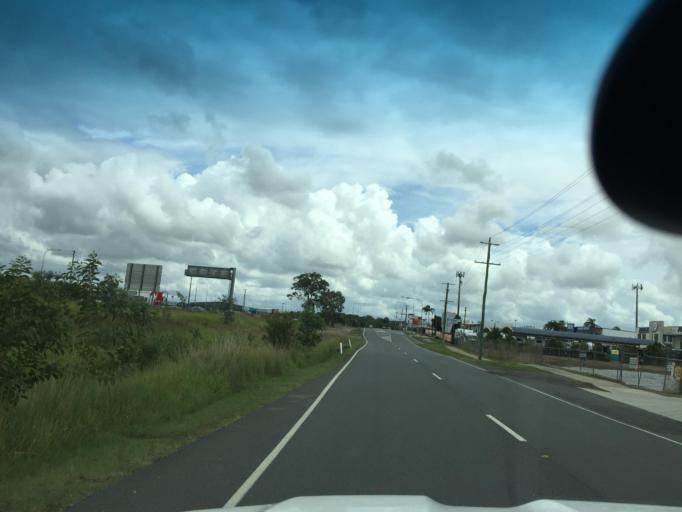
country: AU
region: Queensland
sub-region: Moreton Bay
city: Burpengary
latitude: -27.1630
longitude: 152.9798
